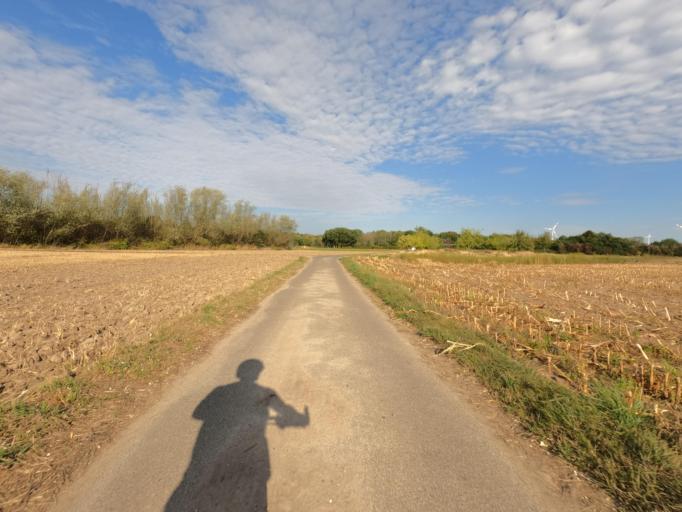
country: DE
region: North Rhine-Westphalia
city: Huckelhoven
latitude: 51.1094
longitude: 6.2373
